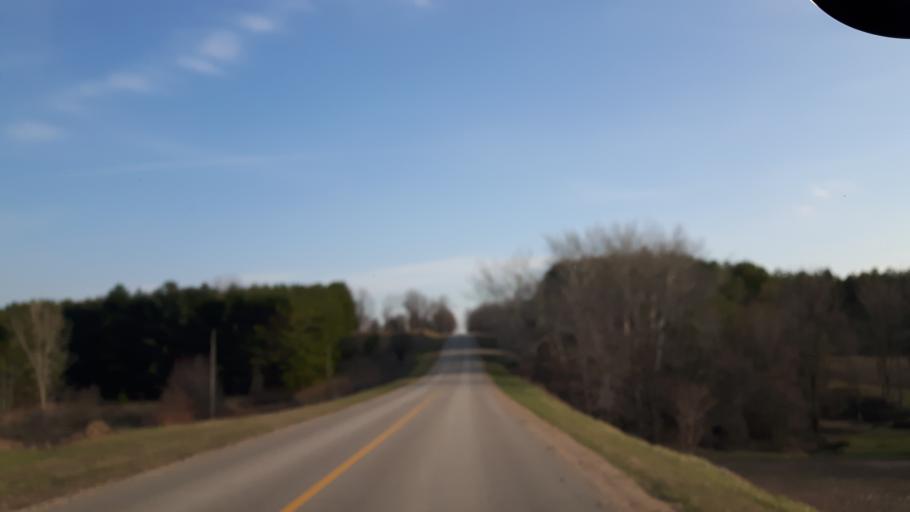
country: CA
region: Ontario
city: Goderich
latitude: 43.6720
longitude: -81.6644
